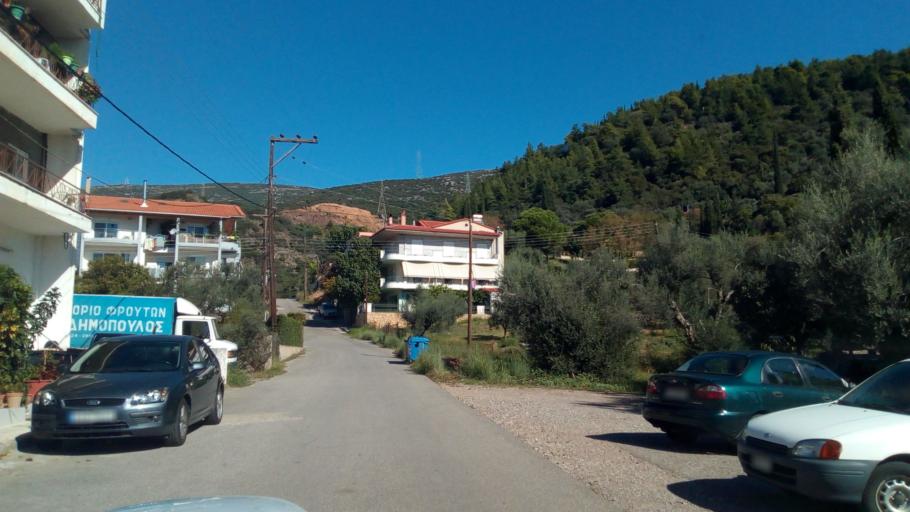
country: GR
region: West Greece
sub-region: Nomos Aitolias kai Akarnanias
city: Nafpaktos
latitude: 38.3939
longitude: 21.8186
